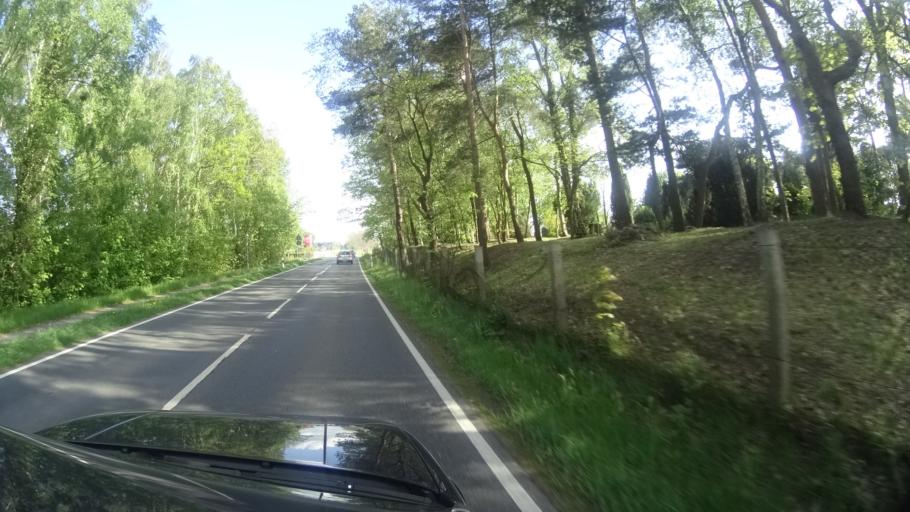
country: DE
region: Mecklenburg-Vorpommern
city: Ostseebad Dierhagen
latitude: 54.2903
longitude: 12.3531
